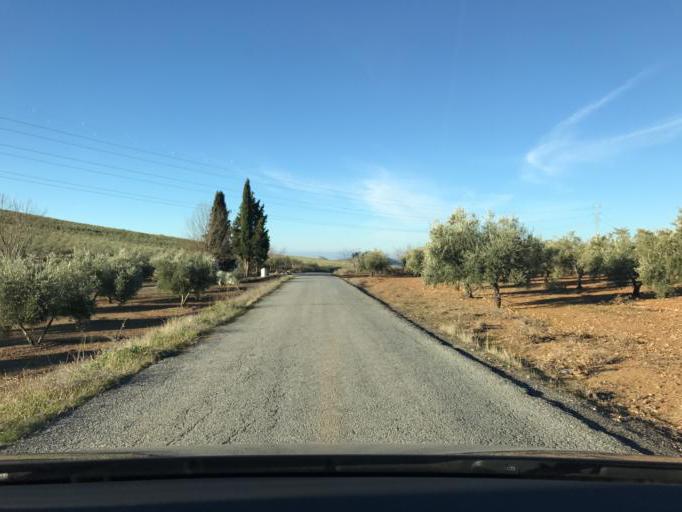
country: ES
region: Andalusia
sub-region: Provincia de Granada
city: Calicasas
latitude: 37.2617
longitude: -3.6214
